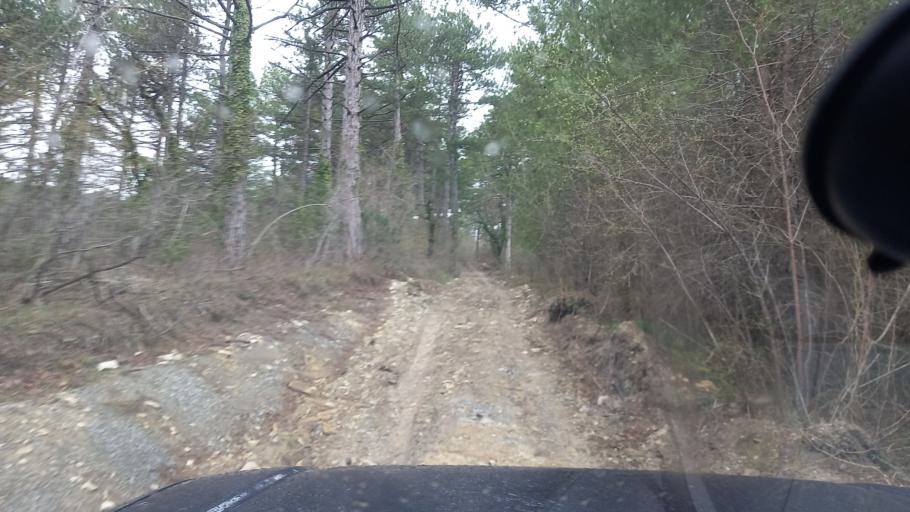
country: RU
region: Krasnodarskiy
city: Arkhipo-Osipovka
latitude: 44.3728
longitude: 38.4731
